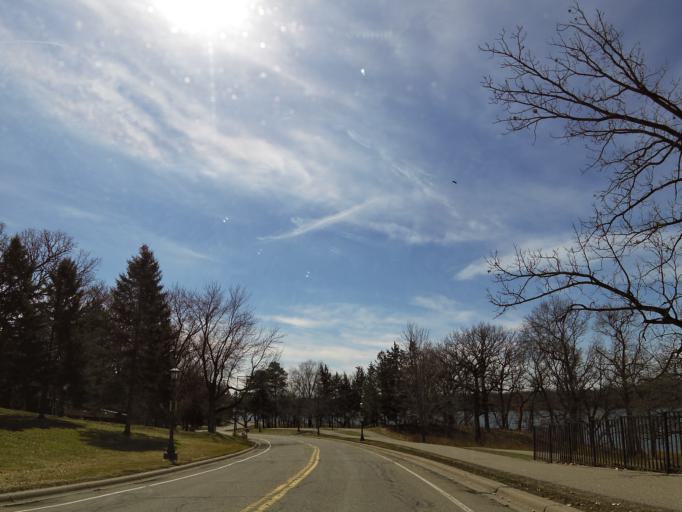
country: US
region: Minnesota
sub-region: Ramsey County
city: Little Canada
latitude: 44.9893
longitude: -93.0514
